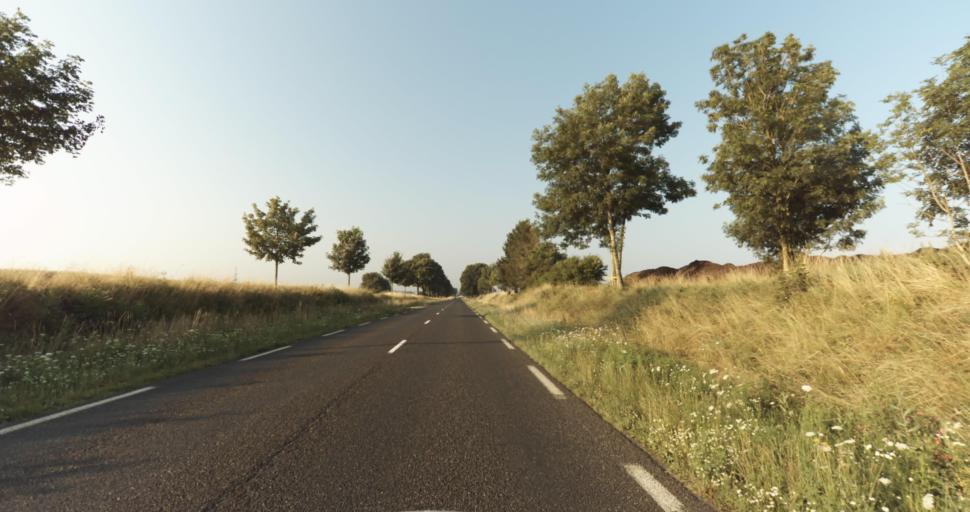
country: FR
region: Lorraine
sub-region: Departement de Meurthe-et-Moselle
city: Briey
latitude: 49.2624
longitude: 5.9509
